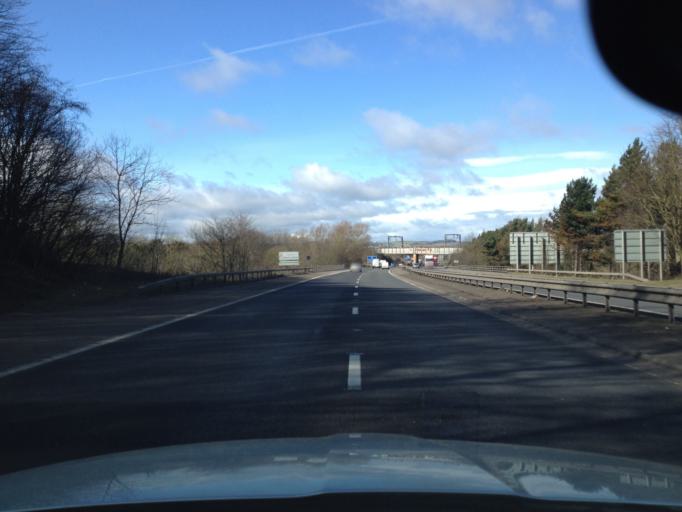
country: GB
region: Scotland
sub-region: Edinburgh
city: Newbridge
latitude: 55.9252
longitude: -3.4263
